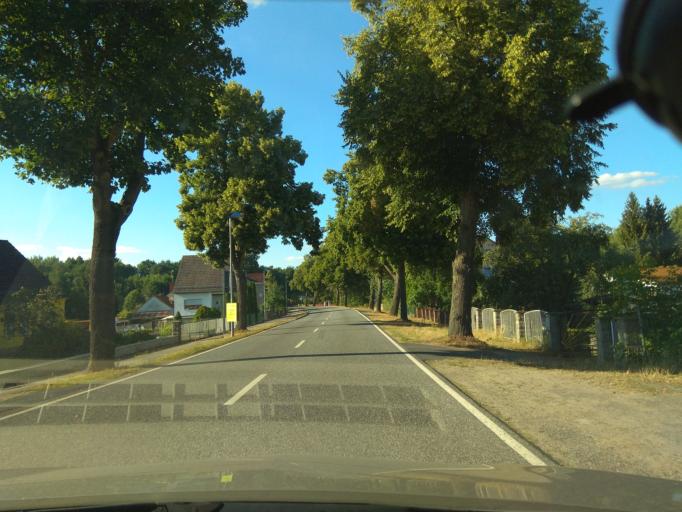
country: DE
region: Brandenburg
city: Zossen
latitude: 52.1478
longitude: 13.4802
